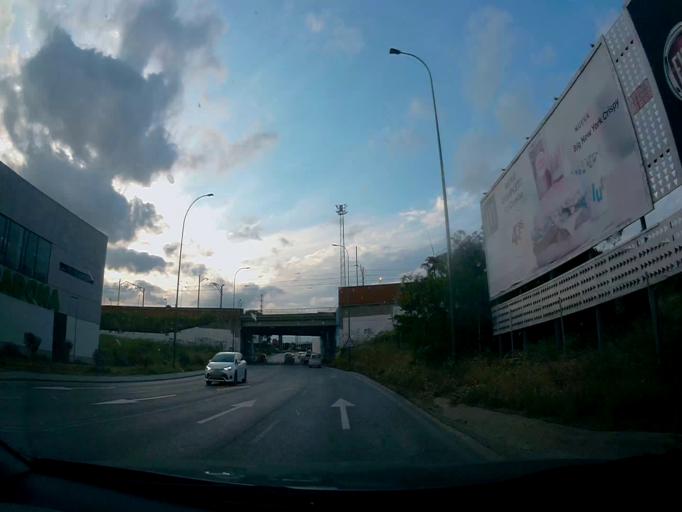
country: ES
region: Madrid
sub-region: Provincia de Madrid
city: Mostoles
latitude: 40.3301
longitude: -3.8826
